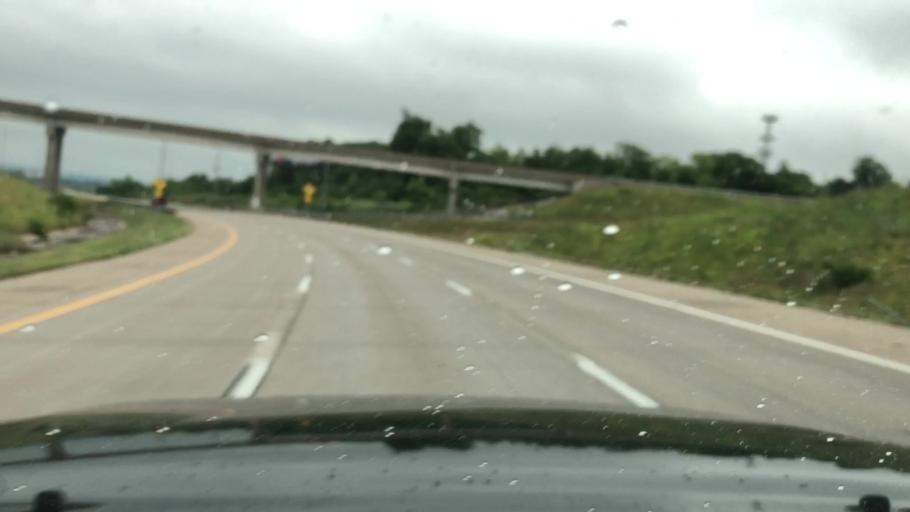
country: US
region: Missouri
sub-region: Saint Charles County
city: Saint Peters
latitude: 38.7998
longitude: -90.5902
